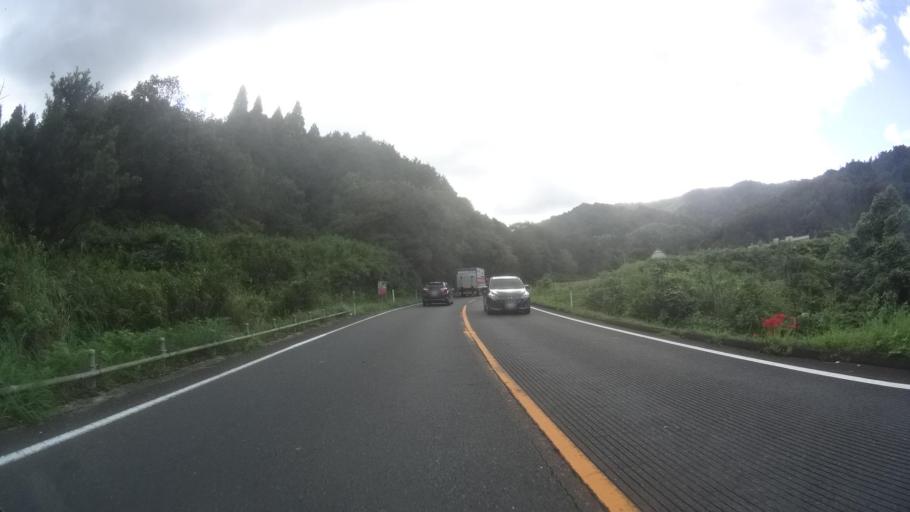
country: JP
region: Kyoto
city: Miyazu
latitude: 35.4600
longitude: 135.0831
